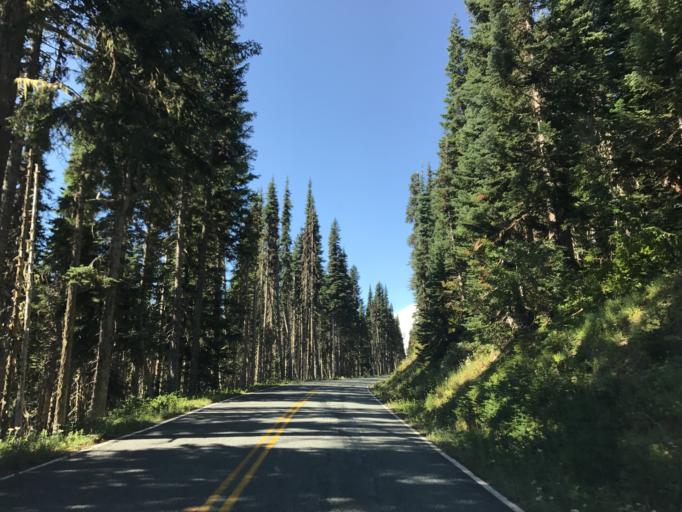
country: US
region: Washington
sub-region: King County
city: Enumclaw
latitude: 46.9192
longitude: -121.5710
